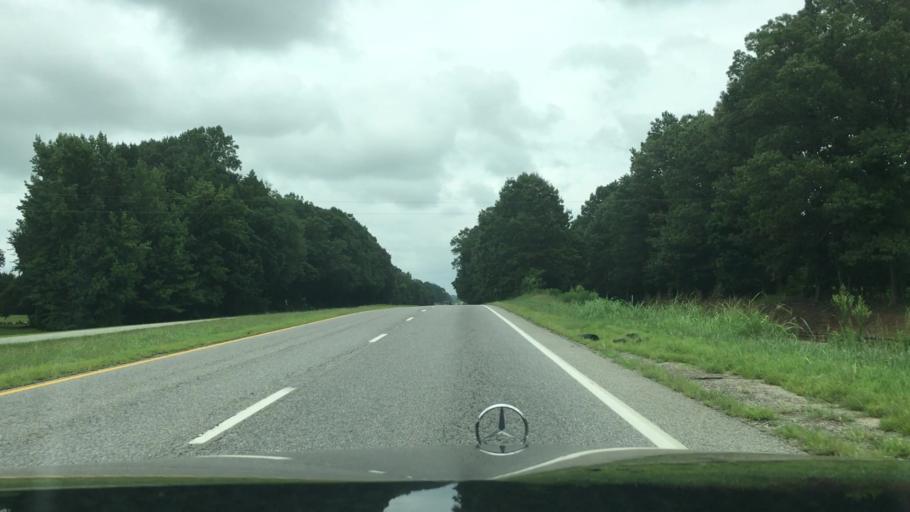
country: US
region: Virginia
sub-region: Amelia County
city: Amelia Court House
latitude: 37.3216
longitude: -78.0368
